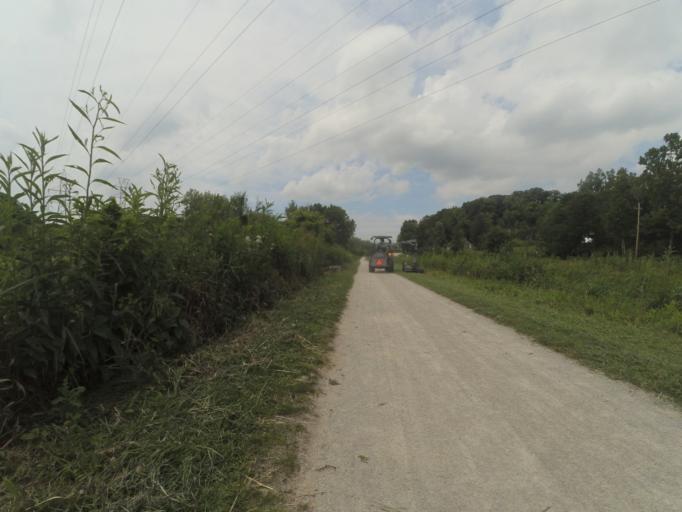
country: US
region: Ohio
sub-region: Cuyahoga County
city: Valley View
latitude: 41.3654
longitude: -81.6095
